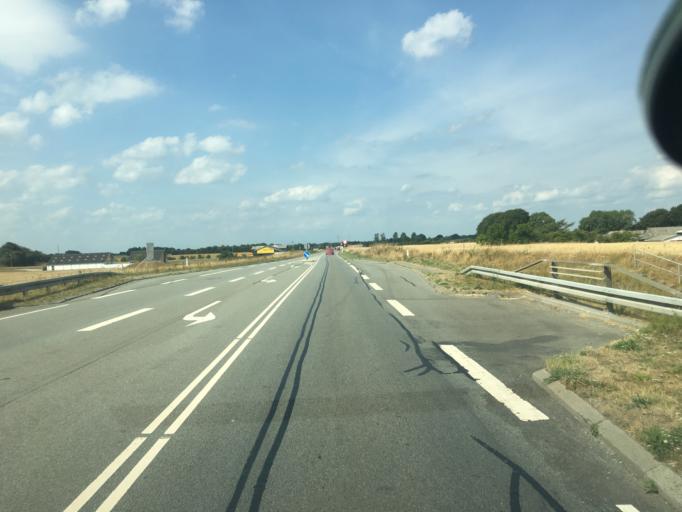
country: DK
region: South Denmark
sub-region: Aabenraa Kommune
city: Krusa
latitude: 54.9392
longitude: 9.3784
